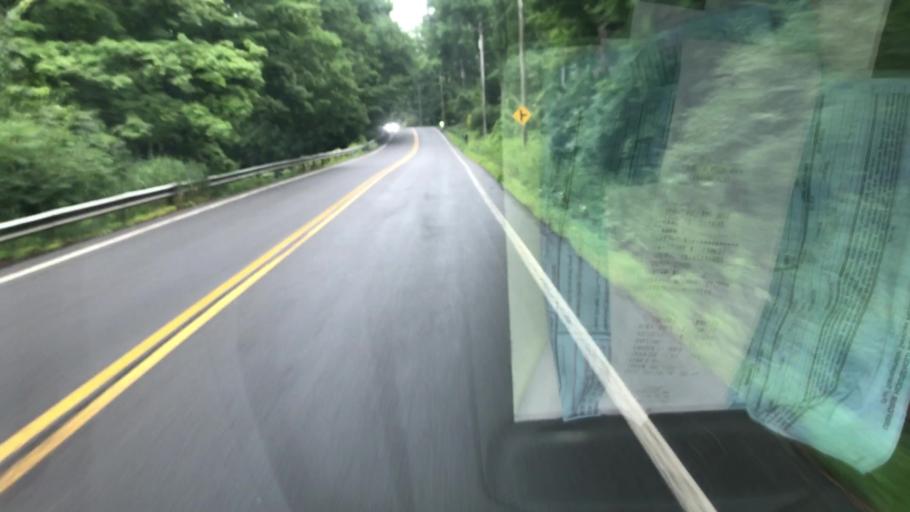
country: US
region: New York
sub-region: Onondaga County
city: Manlius
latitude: 43.0009
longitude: -75.9974
